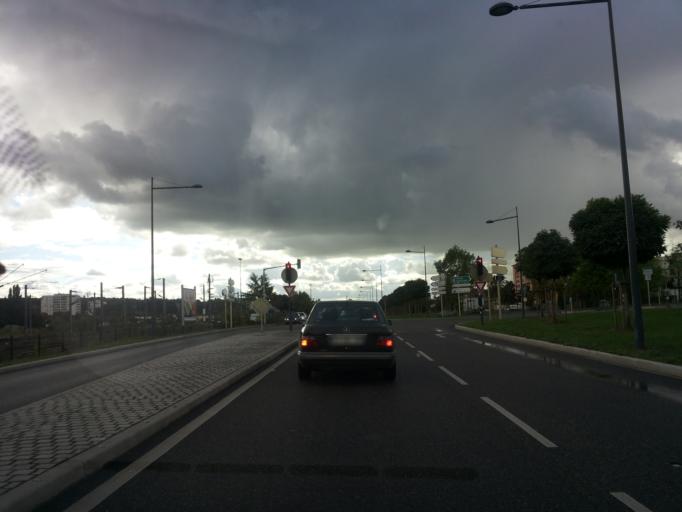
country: FR
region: Alsace
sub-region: Departement du Haut-Rhin
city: Riedisheim
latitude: 47.7515
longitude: 7.3593
